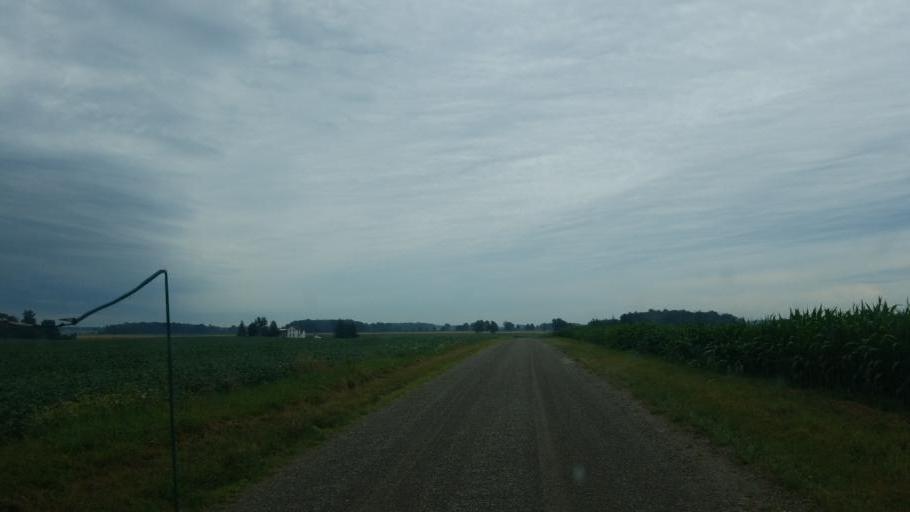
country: US
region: Indiana
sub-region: DeKalb County
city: Butler
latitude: 41.4464
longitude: -84.9098
